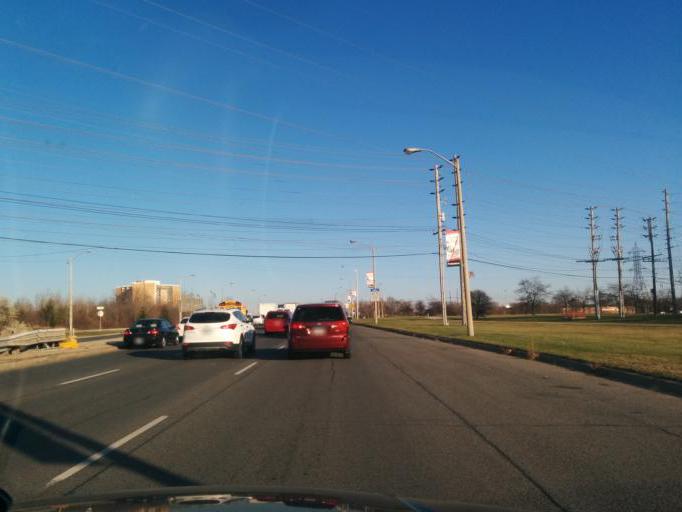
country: CA
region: Ontario
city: Etobicoke
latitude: 43.6741
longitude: -79.5666
